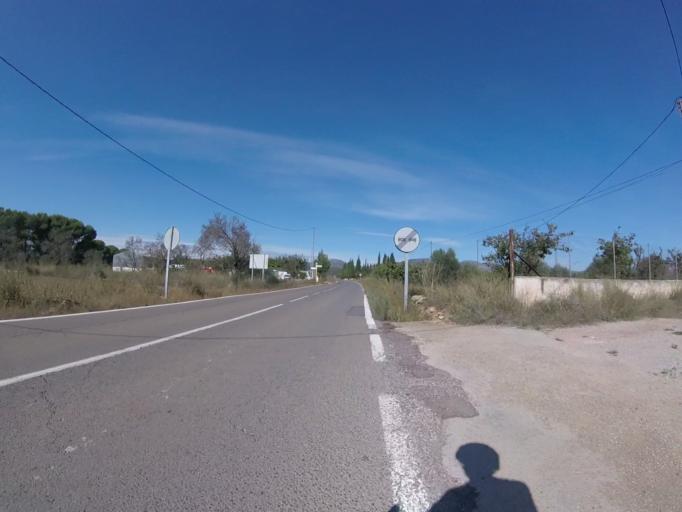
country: ES
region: Valencia
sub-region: Provincia de Castello
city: Benlloch
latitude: 40.2132
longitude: 0.0220
